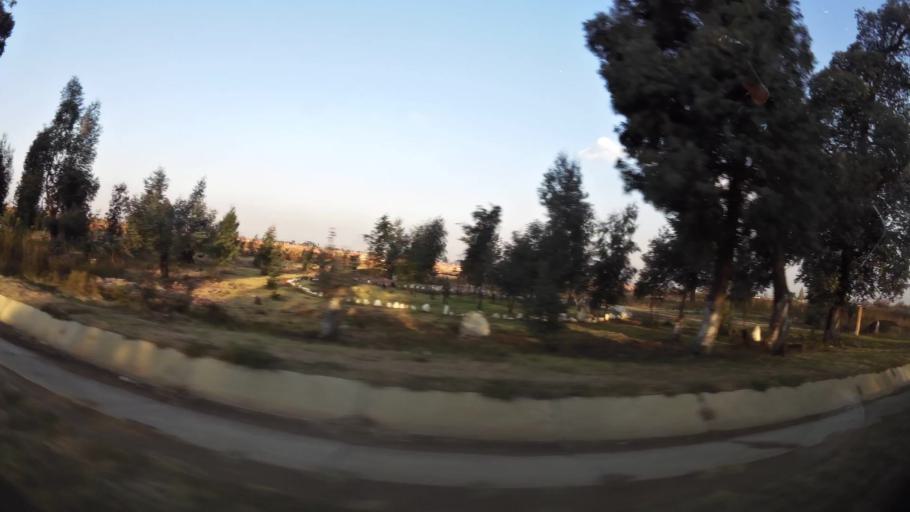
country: ZA
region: Gauteng
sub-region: Ekurhuleni Metropolitan Municipality
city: Benoni
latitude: -26.1493
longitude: 28.3828
